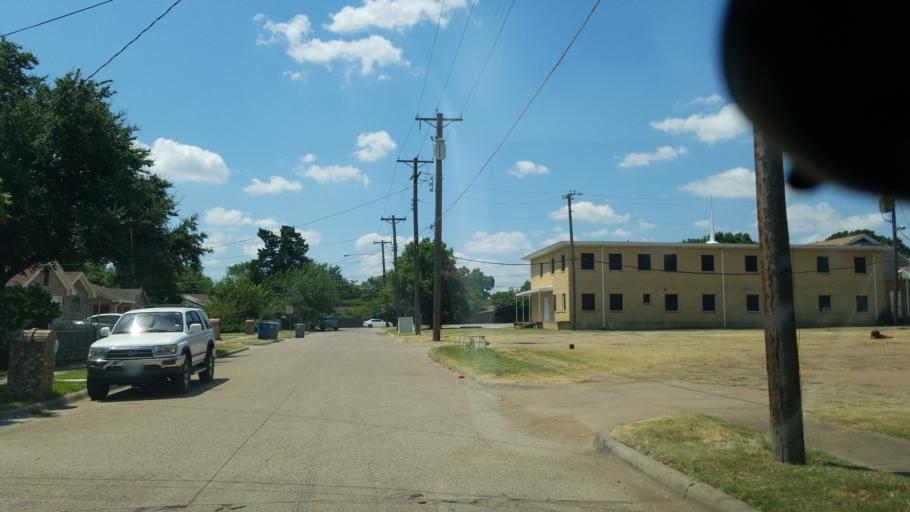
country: US
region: Texas
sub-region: Dallas County
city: Cockrell Hill
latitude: 32.7216
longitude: -96.8379
